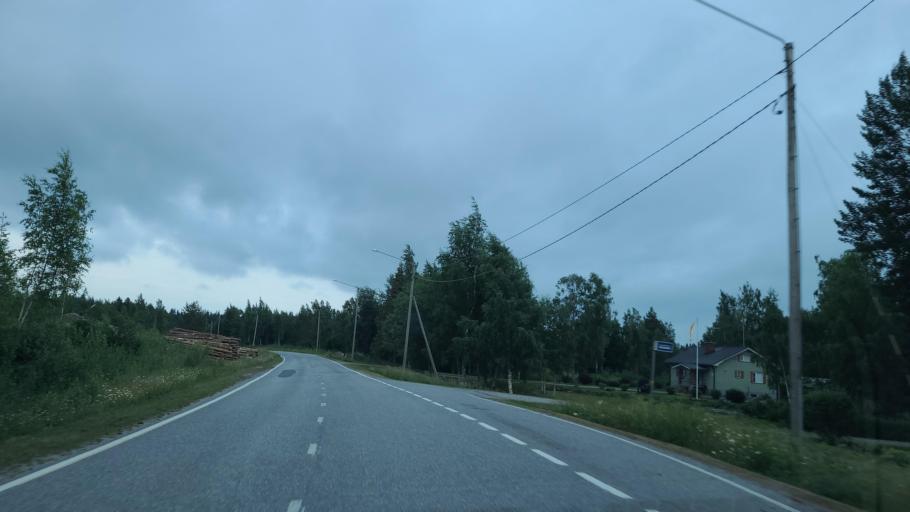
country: FI
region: Ostrobothnia
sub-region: Vaasa
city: Replot
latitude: 63.2822
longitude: 21.1268
